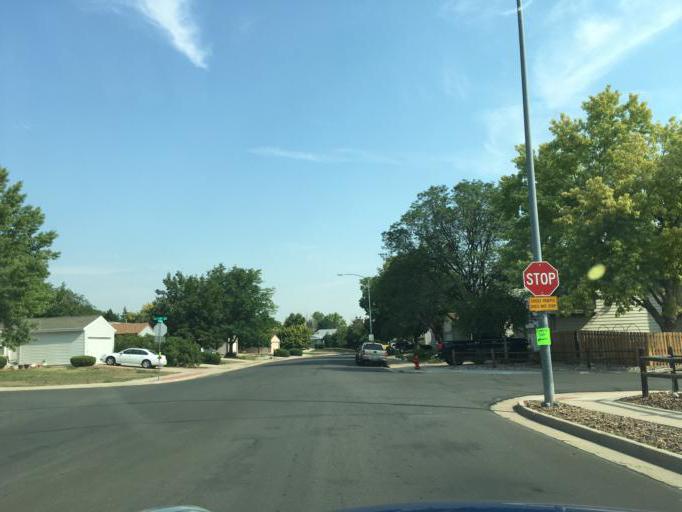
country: US
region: Colorado
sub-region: Adams County
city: Westminster
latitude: 39.8309
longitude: -105.0588
